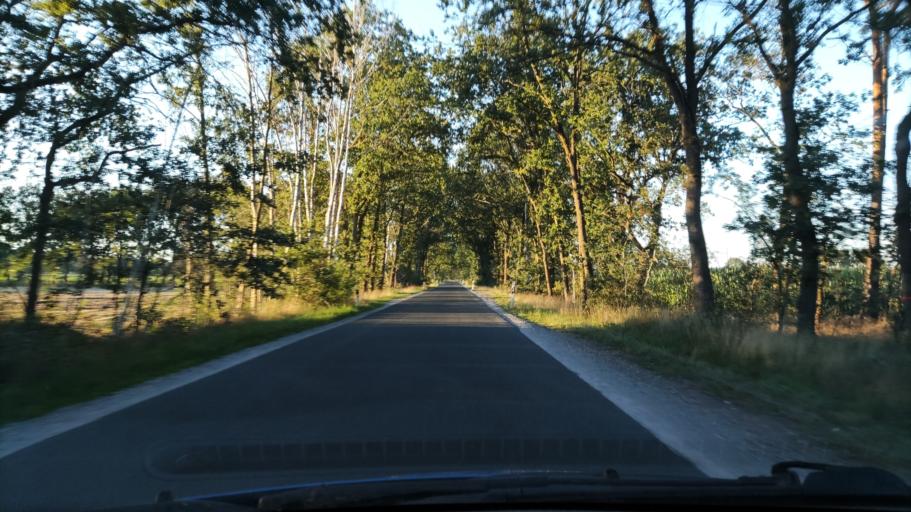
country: DE
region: Lower Saxony
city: Klein Gusborn
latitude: 53.0690
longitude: 11.1890
